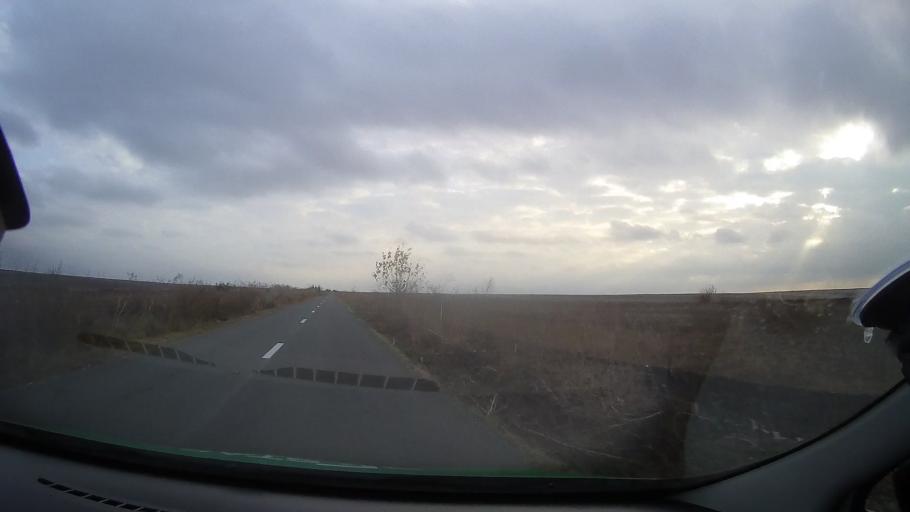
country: RO
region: Constanta
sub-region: Comuna Pestera
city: Pestera
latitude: 44.1482
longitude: 28.1147
